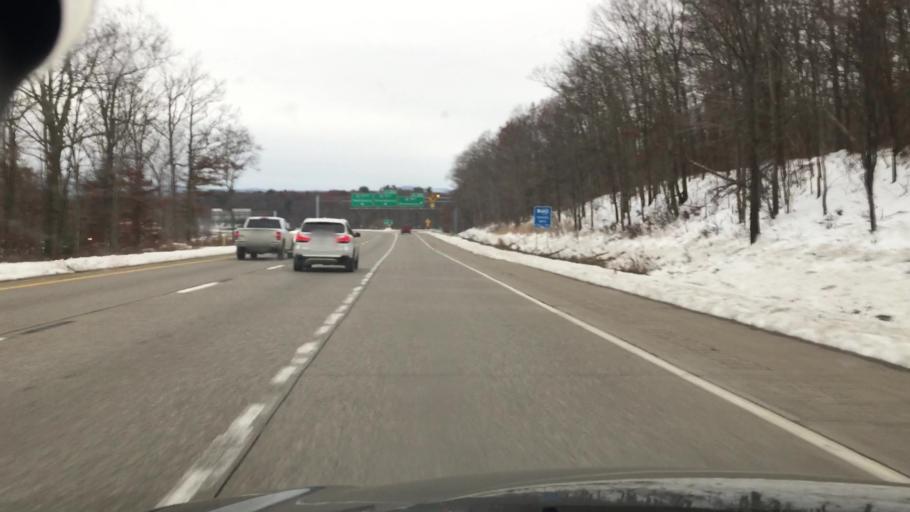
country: US
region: Pennsylvania
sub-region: Luzerne County
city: Conyngham
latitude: 41.0512
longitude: -76.0086
